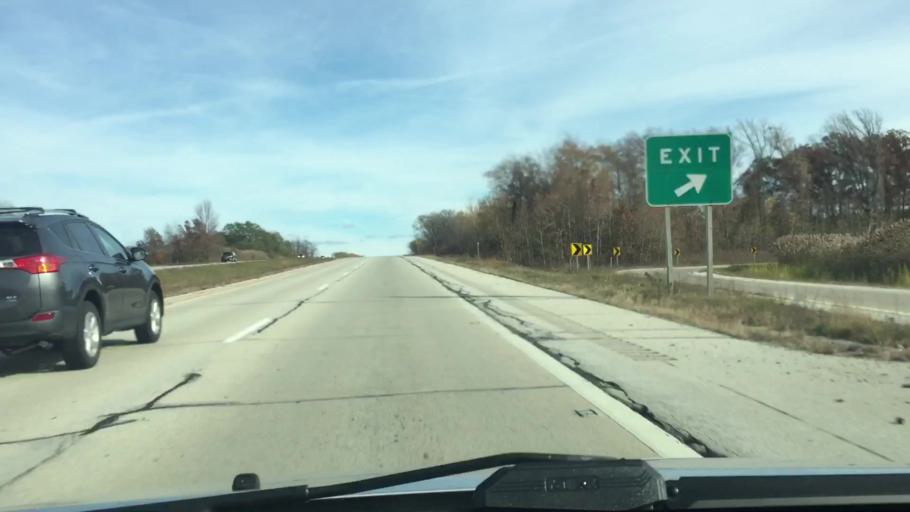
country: US
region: Wisconsin
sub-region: Brown County
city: Bellevue
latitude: 44.5242
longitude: -87.9061
